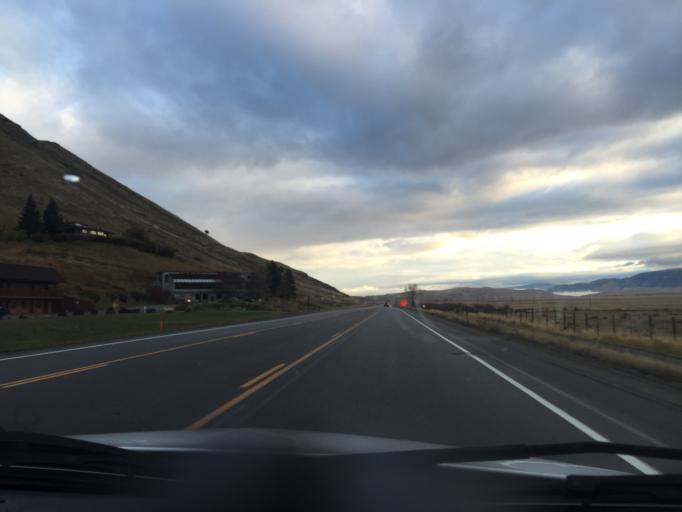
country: US
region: Wyoming
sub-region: Teton County
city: Jackson
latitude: 43.5070
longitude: -110.7560
